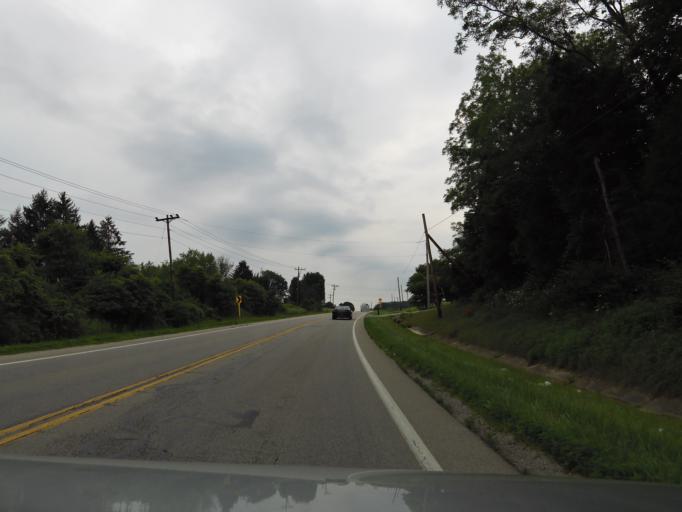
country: US
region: Ohio
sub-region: Brown County
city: Georgetown
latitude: 38.9301
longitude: -83.9013
